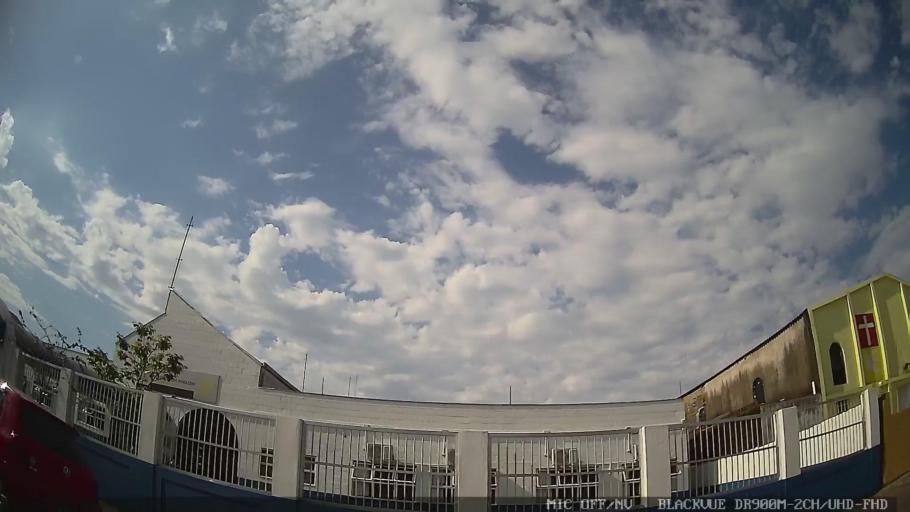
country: BR
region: Sao Paulo
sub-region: Guaruja
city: Guaruja
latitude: -23.9629
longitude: -46.2525
